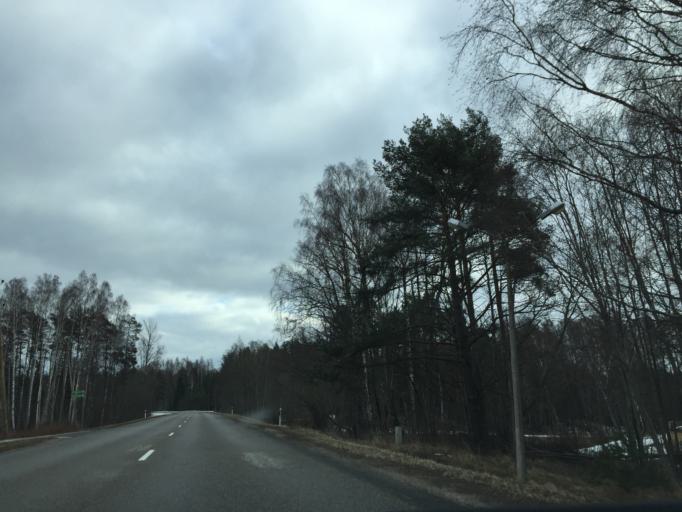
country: LV
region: Salacgrivas
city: Ainazi
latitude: 57.8570
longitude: 24.5134
